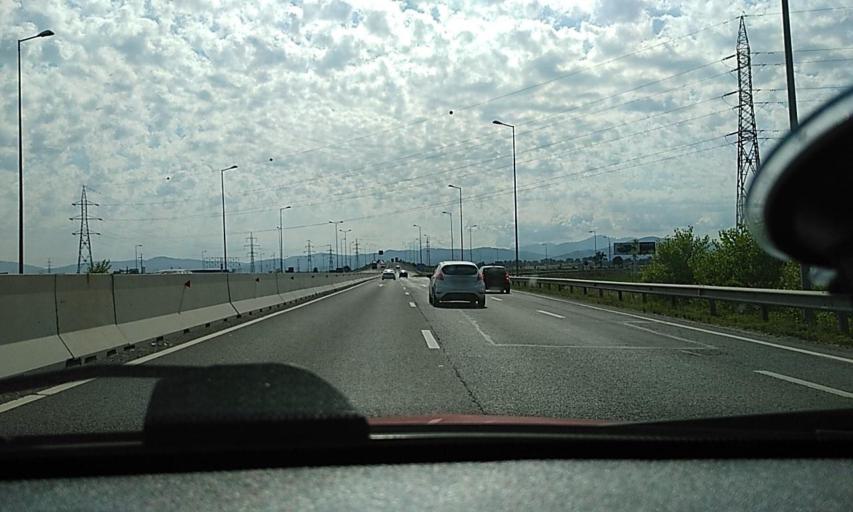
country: RO
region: Brasov
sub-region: Comuna Sanpetru
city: Sanpetru
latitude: 45.6825
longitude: 25.6541
